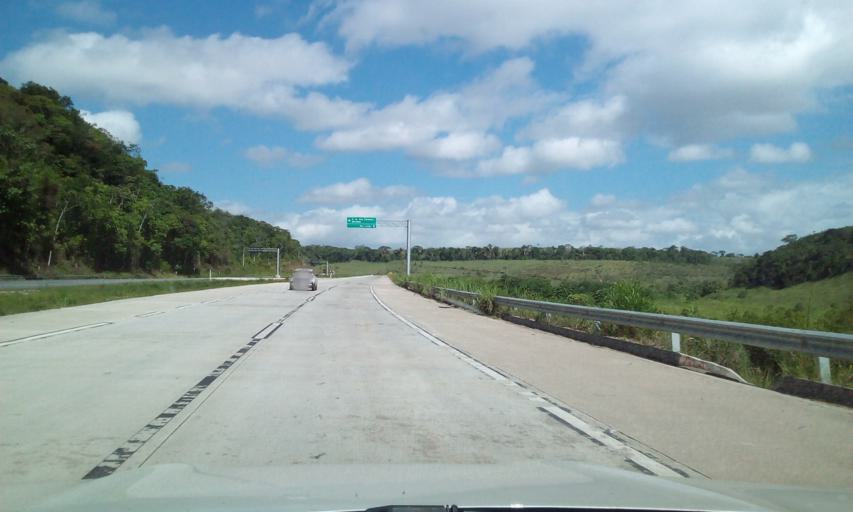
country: BR
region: Alagoas
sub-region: Rio Largo
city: Rio Largo
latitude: -9.5032
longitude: -35.9150
